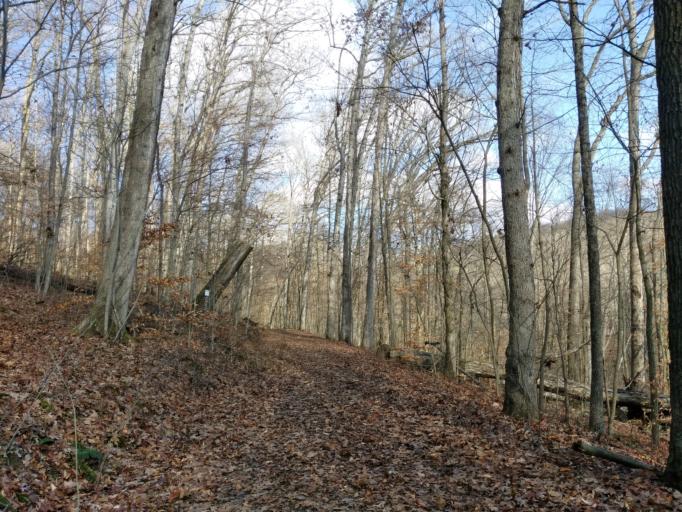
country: US
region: Ohio
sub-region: Fairfield County
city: Lancaster
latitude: 39.6449
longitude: -82.6452
